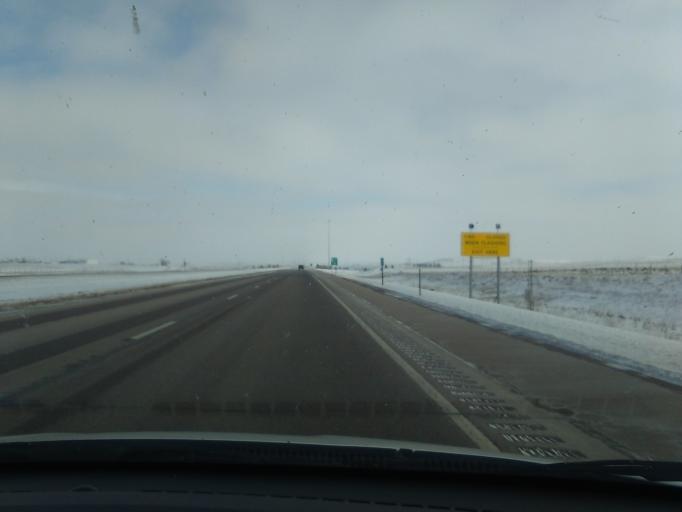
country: US
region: Nebraska
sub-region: Kimball County
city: Kimball
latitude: 41.2148
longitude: -103.6771
